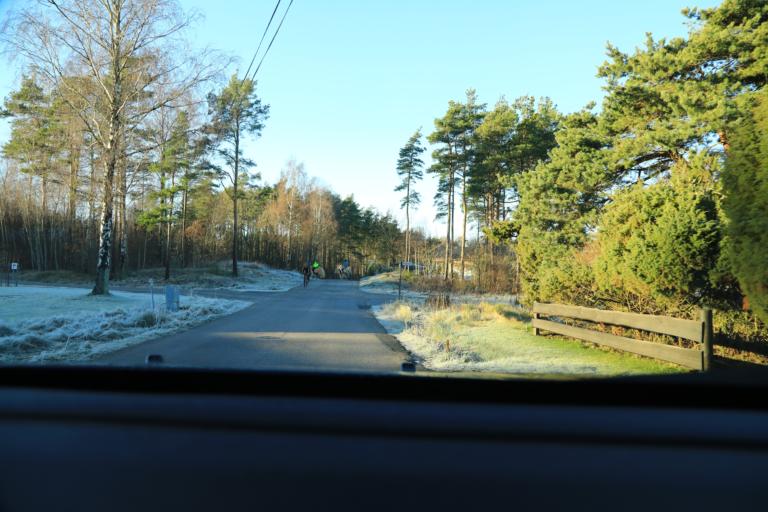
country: SE
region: Halland
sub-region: Varbergs Kommun
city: Varberg
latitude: 57.2015
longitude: 12.1911
